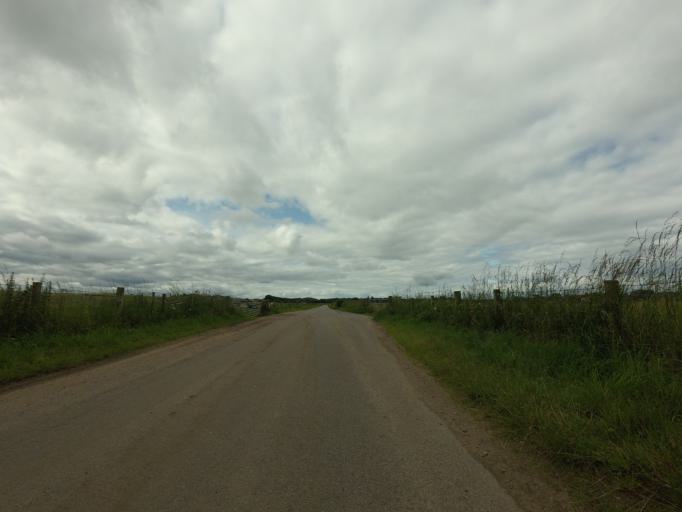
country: GB
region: Scotland
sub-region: Moray
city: Kinloss
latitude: 57.6301
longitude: -3.5416
